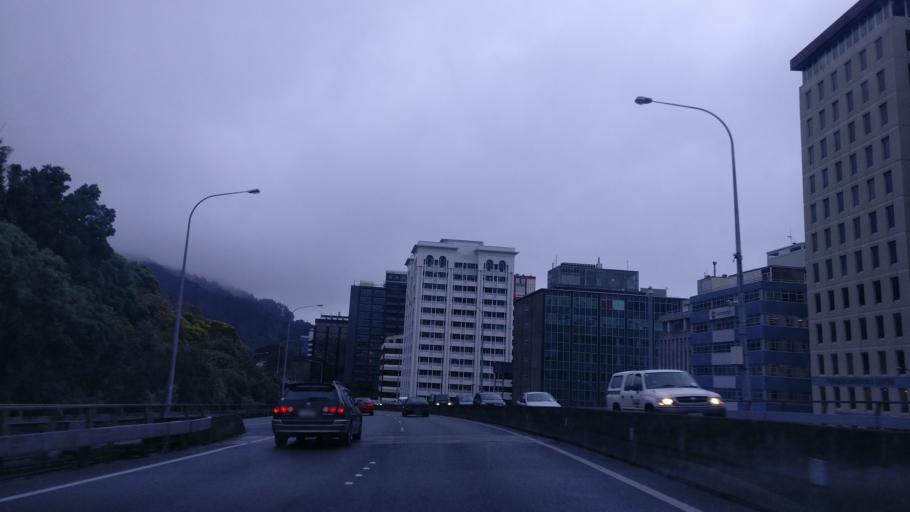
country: NZ
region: Wellington
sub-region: Wellington City
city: Wellington
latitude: -41.2837
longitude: 174.7735
